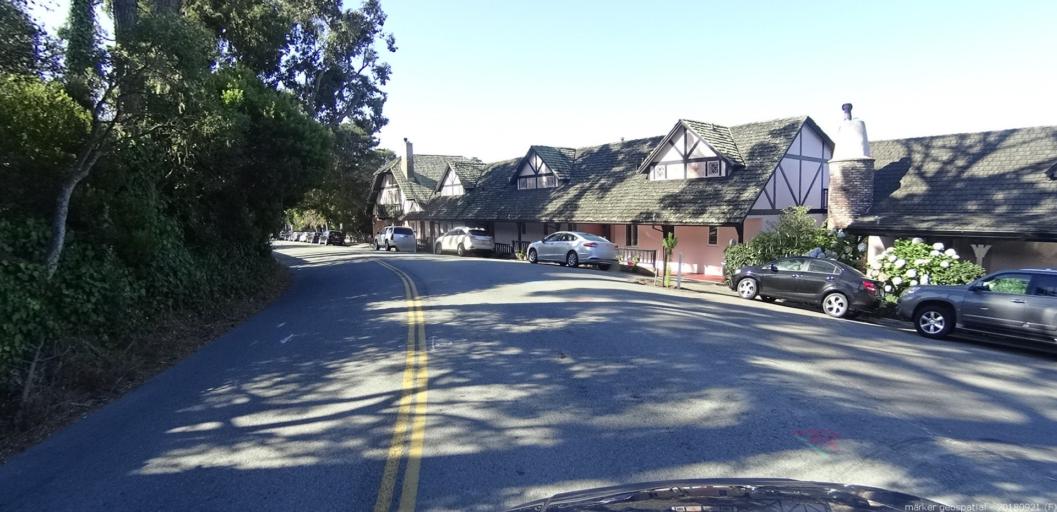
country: US
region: California
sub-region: Monterey County
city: Carmel-by-the-Sea
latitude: 36.5592
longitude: -121.9216
